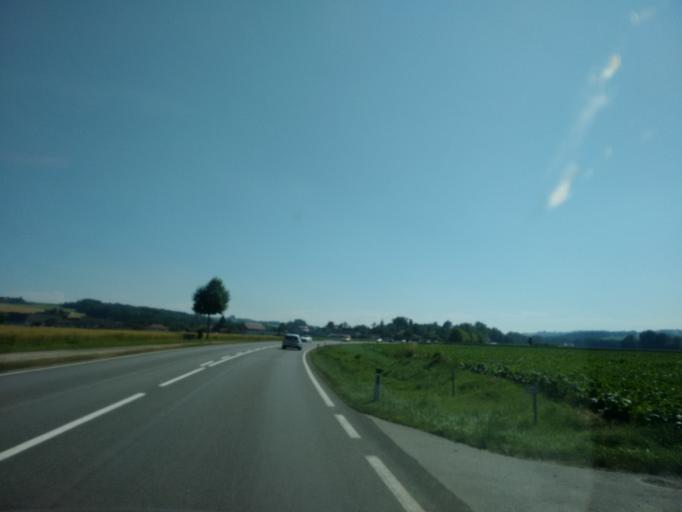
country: AT
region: Upper Austria
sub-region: Wels-Land
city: Buchkirchen
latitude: 48.2849
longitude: 14.0058
